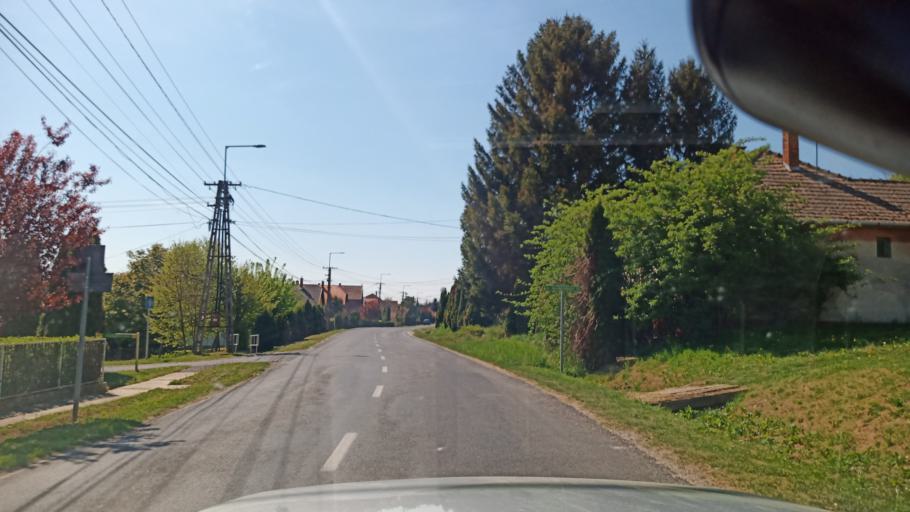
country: HU
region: Zala
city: Sarmellek
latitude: 46.7507
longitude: 17.1074
